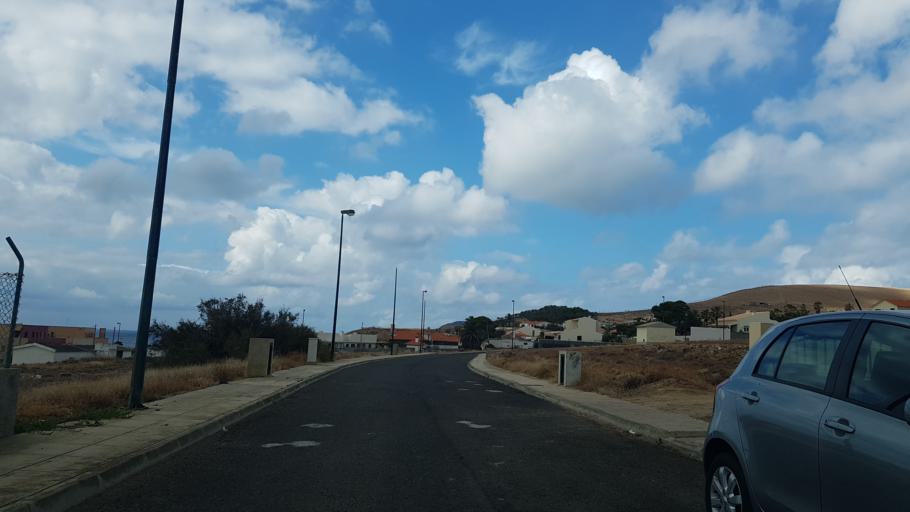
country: PT
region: Madeira
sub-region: Porto Santo
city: Vila de Porto Santo
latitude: 33.0425
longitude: -16.3596
